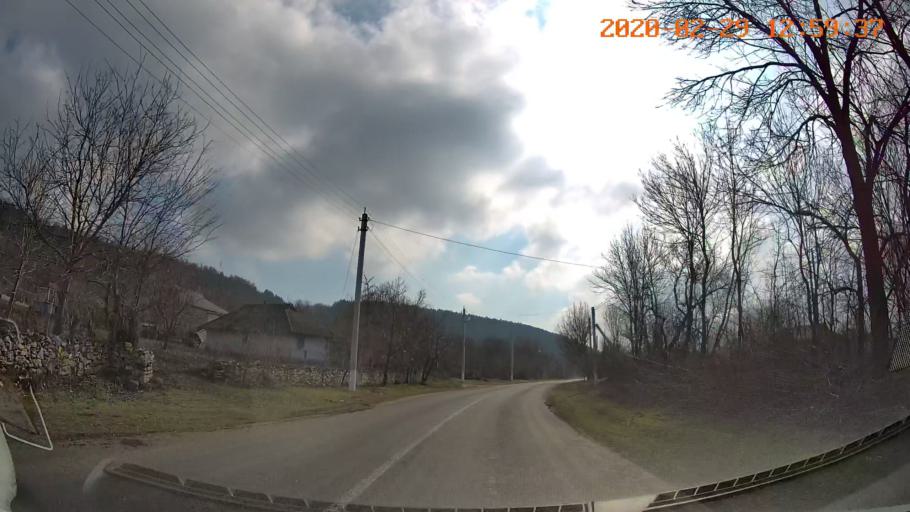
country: MD
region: Telenesti
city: Camenca
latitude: 48.0603
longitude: 28.7251
